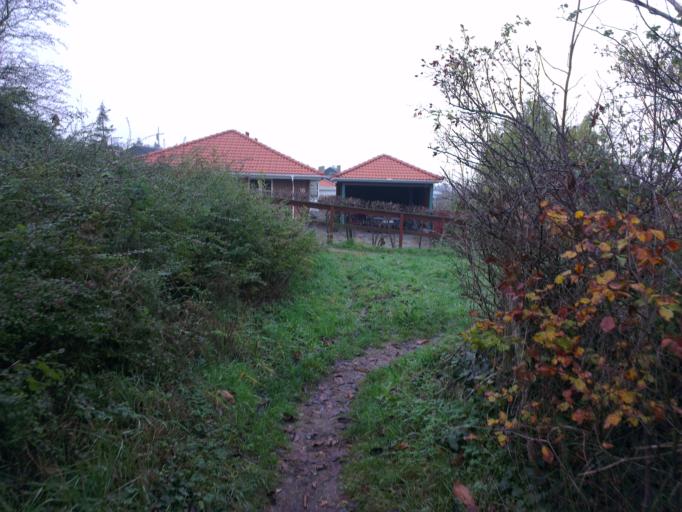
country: DK
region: Capital Region
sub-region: Frederikssund Kommune
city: Jaegerspris
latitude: 55.8525
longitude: 11.9986
